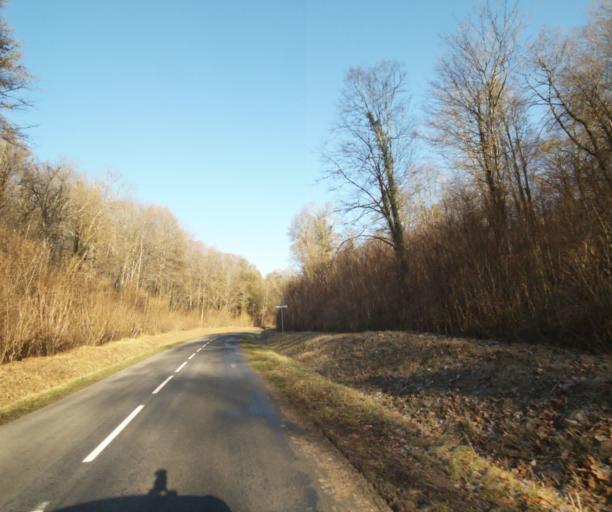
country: FR
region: Champagne-Ardenne
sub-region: Departement de la Haute-Marne
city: Chevillon
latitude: 48.5368
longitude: 5.1933
